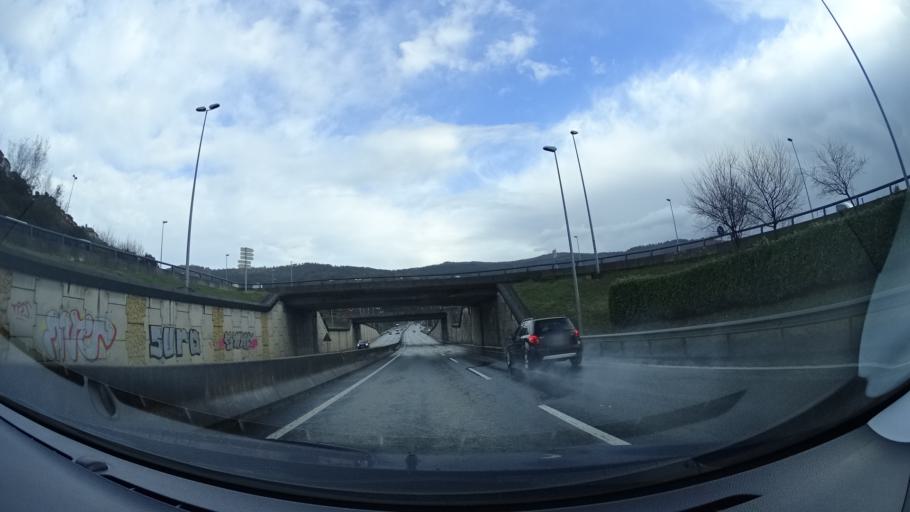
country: ES
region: Basque Country
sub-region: Bizkaia
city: Santutxu
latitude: 43.2500
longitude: -2.9021
